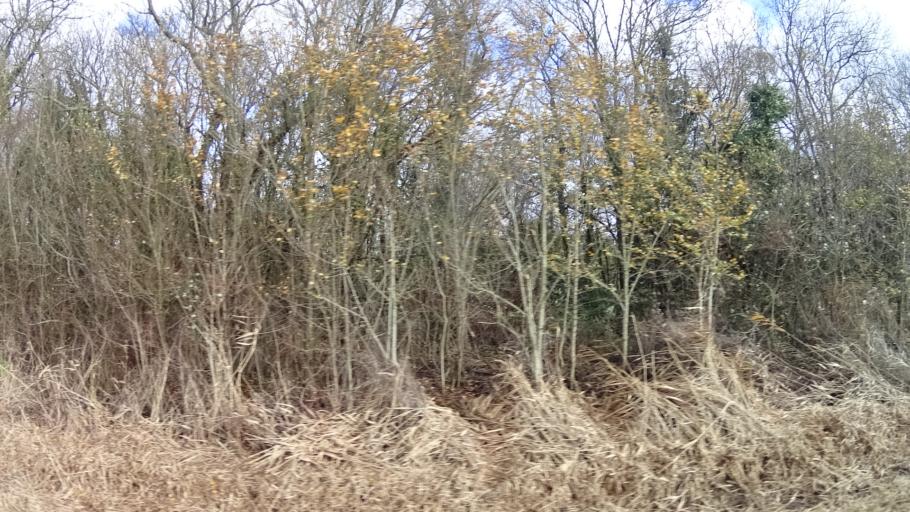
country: FR
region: Brittany
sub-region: Departement du Morbihan
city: Rieux
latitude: 47.5882
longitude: -2.0848
